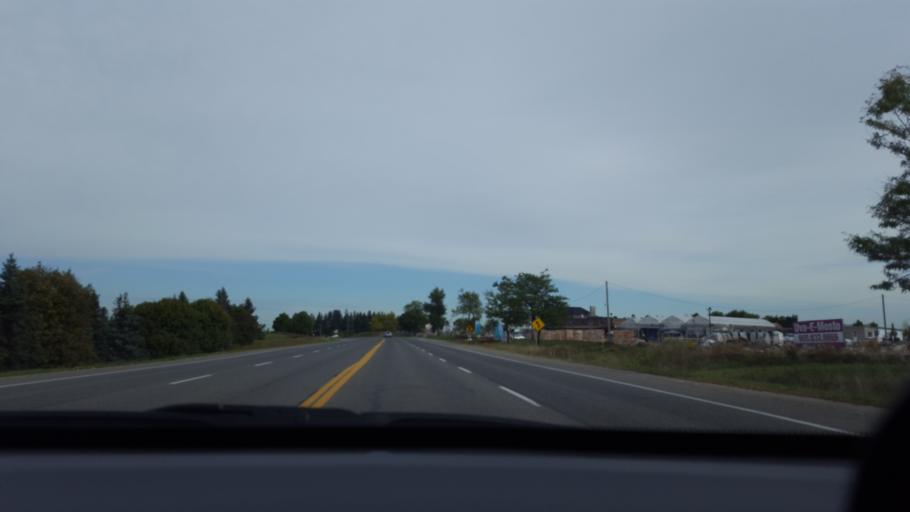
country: CA
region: Ontario
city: Vaughan
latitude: 43.9069
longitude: -79.5234
